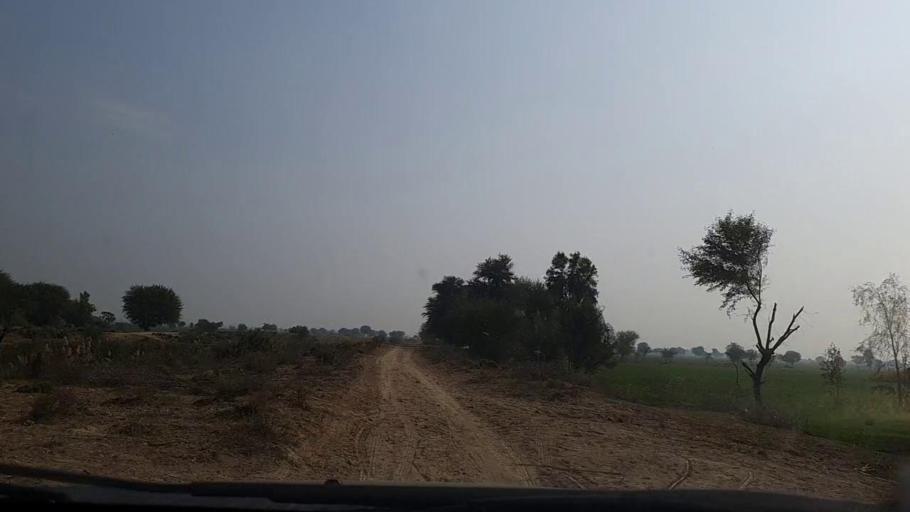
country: PK
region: Sindh
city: Sanghar
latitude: 26.0405
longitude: 68.9951
